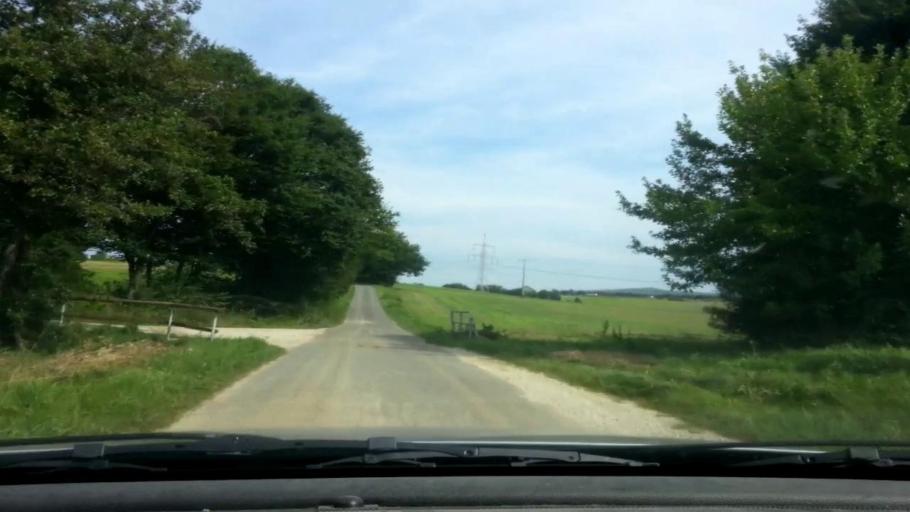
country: DE
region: Bavaria
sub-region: Upper Franconia
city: Memmelsdorf
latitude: 49.9585
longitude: 10.9733
